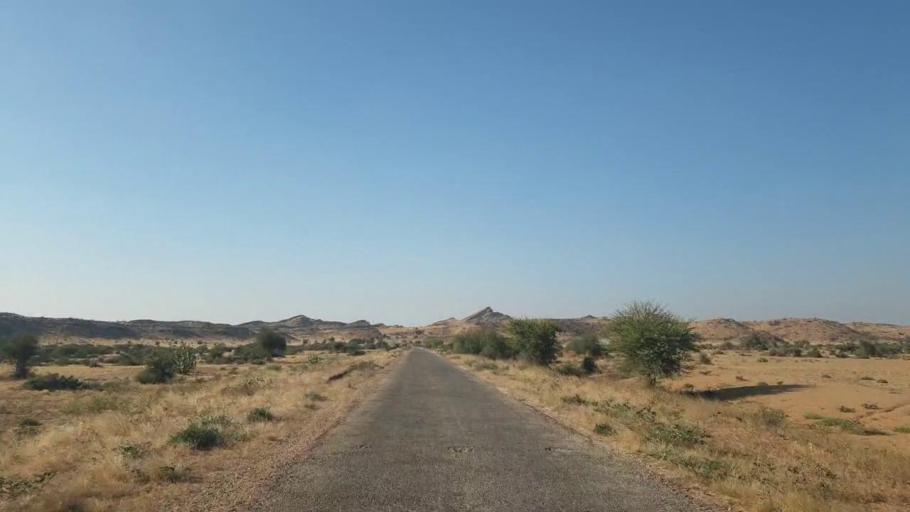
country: PK
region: Sindh
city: Malir Cantonment
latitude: 25.3985
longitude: 67.4925
